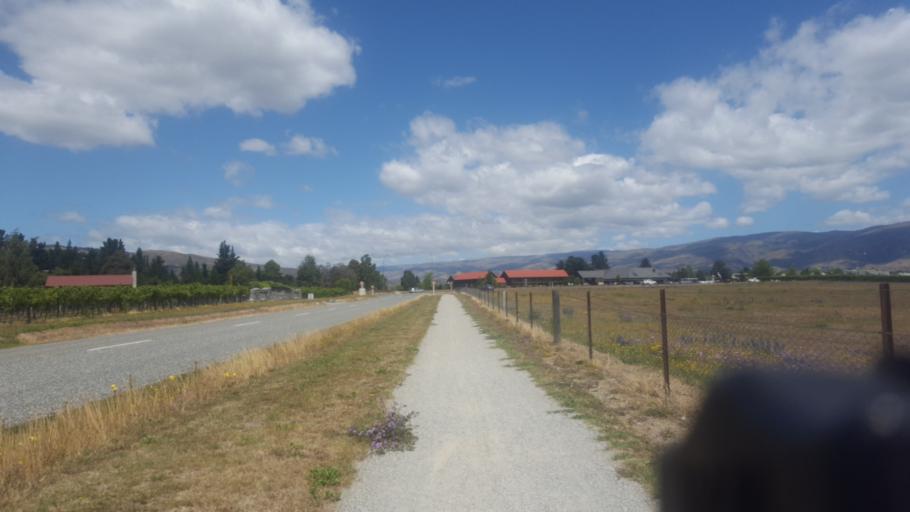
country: NZ
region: Otago
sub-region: Queenstown-Lakes District
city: Wanaka
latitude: -45.0330
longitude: 169.2027
